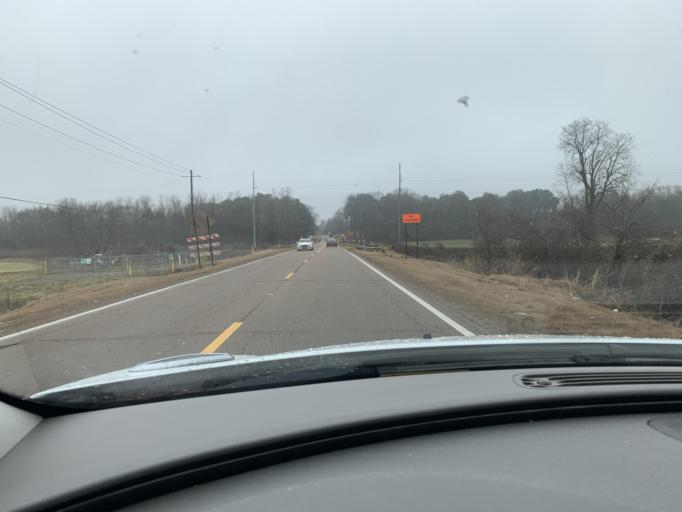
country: US
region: Mississippi
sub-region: De Soto County
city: Hernando
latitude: 34.8708
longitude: -89.9955
